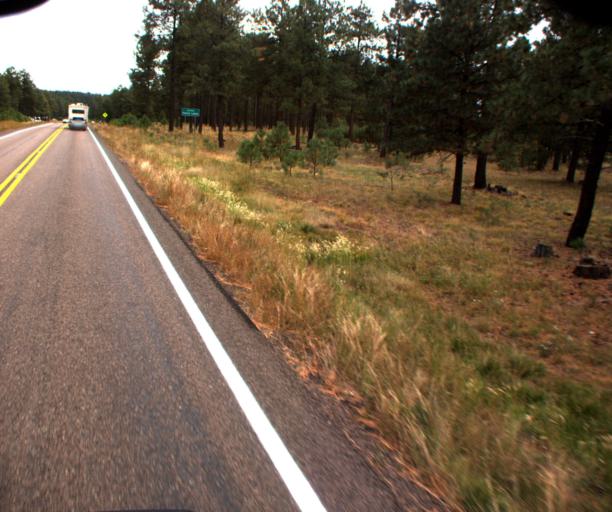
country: US
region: Arizona
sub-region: Navajo County
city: Heber-Overgaard
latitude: 34.3291
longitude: -110.8072
